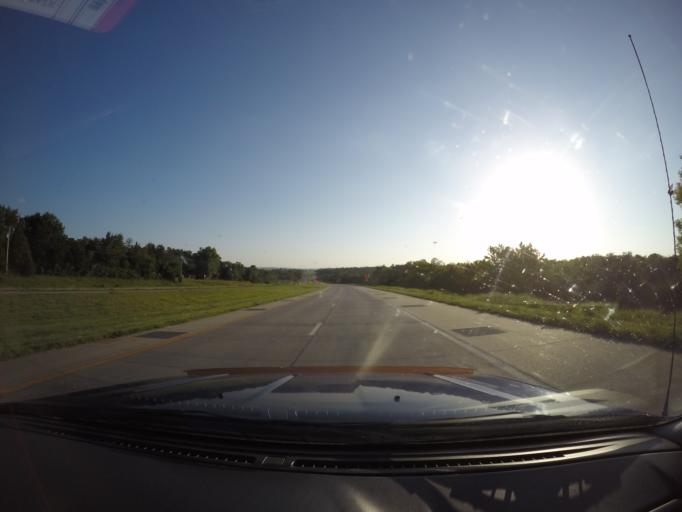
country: US
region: Kansas
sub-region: Pottawatomie County
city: Wamego
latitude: 39.2090
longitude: -96.4158
